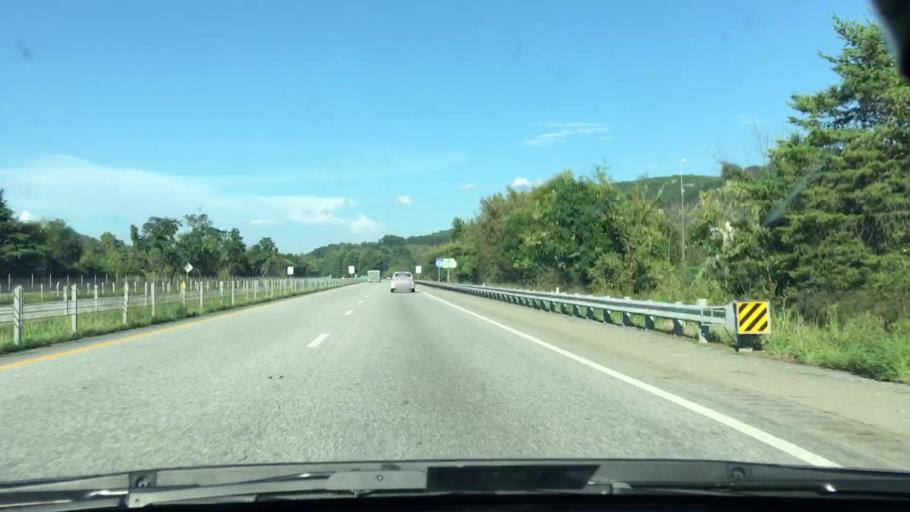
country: US
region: Virginia
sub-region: Alleghany County
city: Clifton Forge
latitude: 37.7946
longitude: -79.8788
